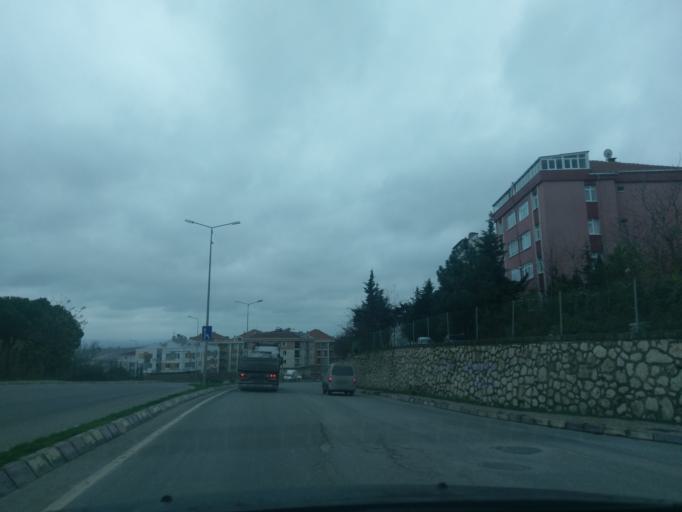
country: TR
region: Istanbul
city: Catalca
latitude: 41.1440
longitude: 28.4682
